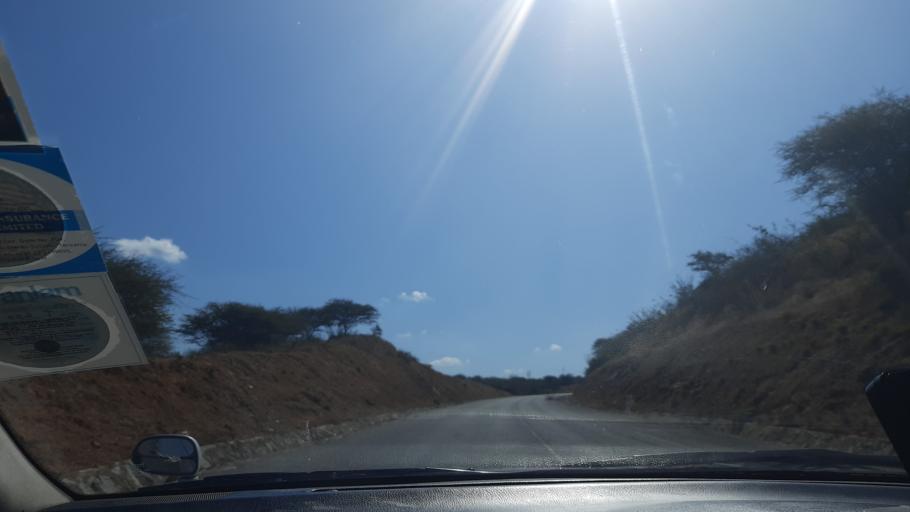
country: TZ
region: Singida
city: Kilimatinde
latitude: -5.7813
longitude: 34.8841
